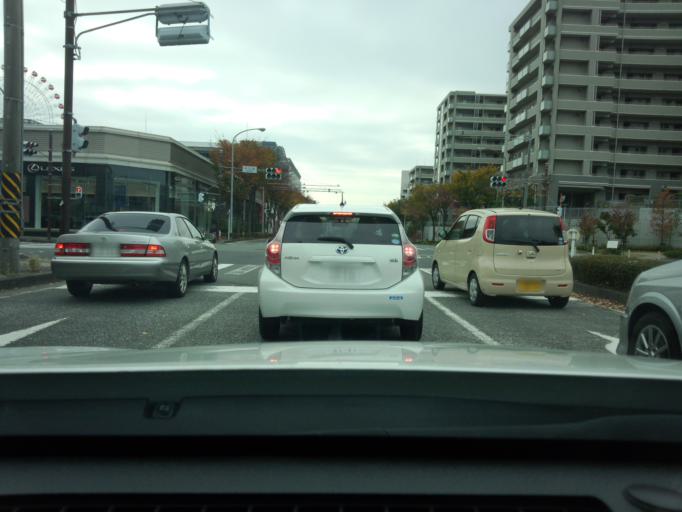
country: JP
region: Tokyo
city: Chofugaoka
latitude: 35.5571
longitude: 139.5779
